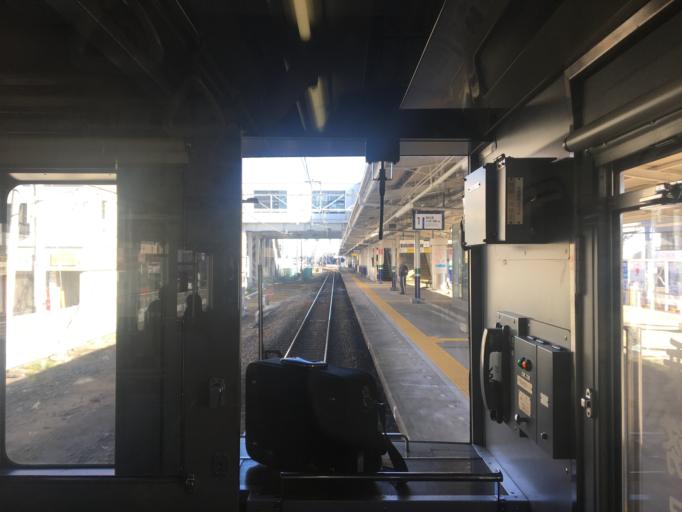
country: JP
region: Saitama
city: Sakado
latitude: 35.9717
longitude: 139.3964
